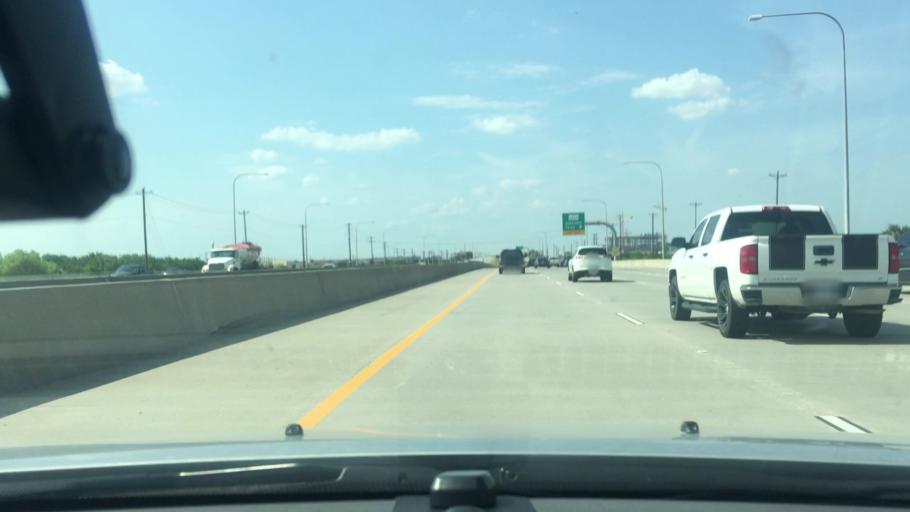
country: US
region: Texas
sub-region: Collin County
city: Frisco
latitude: 33.1673
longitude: -96.8398
